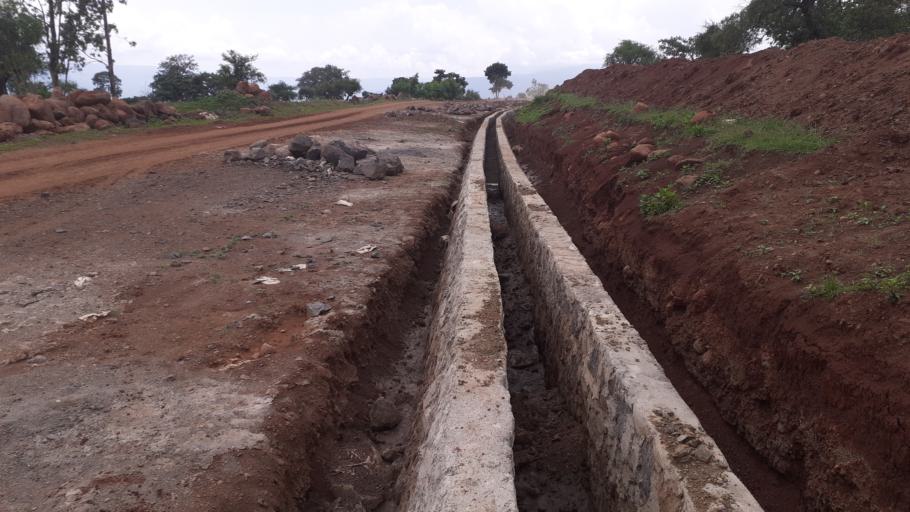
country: ET
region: Southern Nations, Nationalities, and People's Region
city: Areka
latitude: 7.5384
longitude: 37.4940
